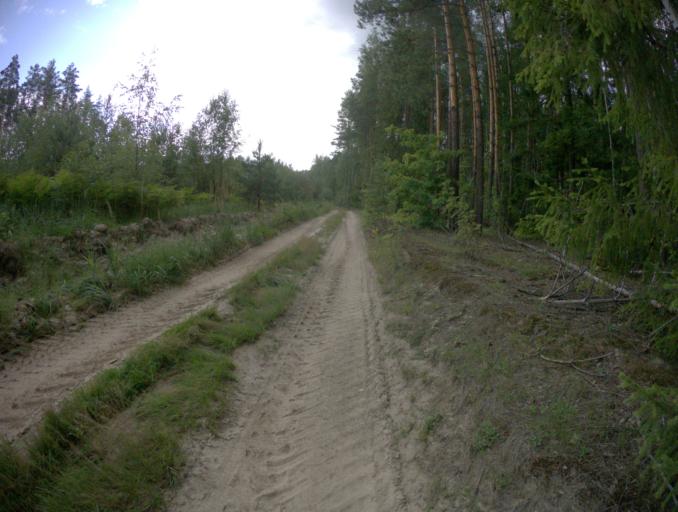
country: RU
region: Vladimir
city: Vorsha
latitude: 55.9539
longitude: 40.1478
